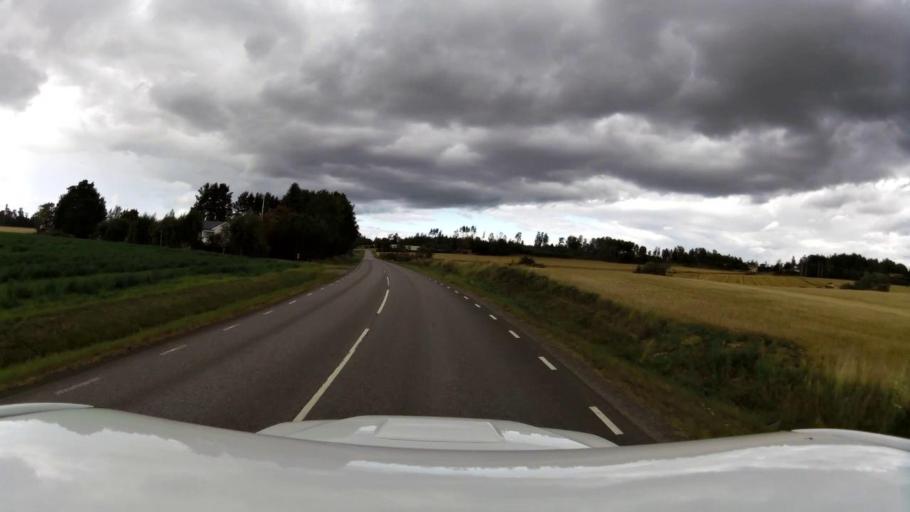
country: SE
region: OEstergoetland
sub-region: Linkopings Kommun
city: Linghem
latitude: 58.3990
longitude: 15.7666
